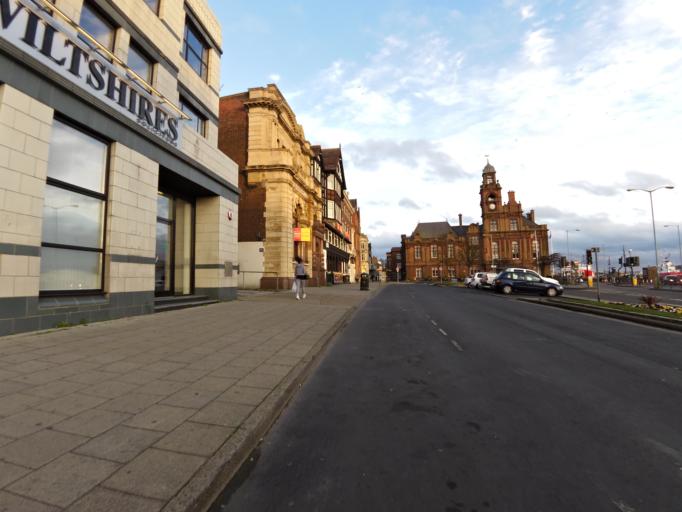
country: GB
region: England
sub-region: Norfolk
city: Great Yarmouth
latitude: 52.6068
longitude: 1.7241
